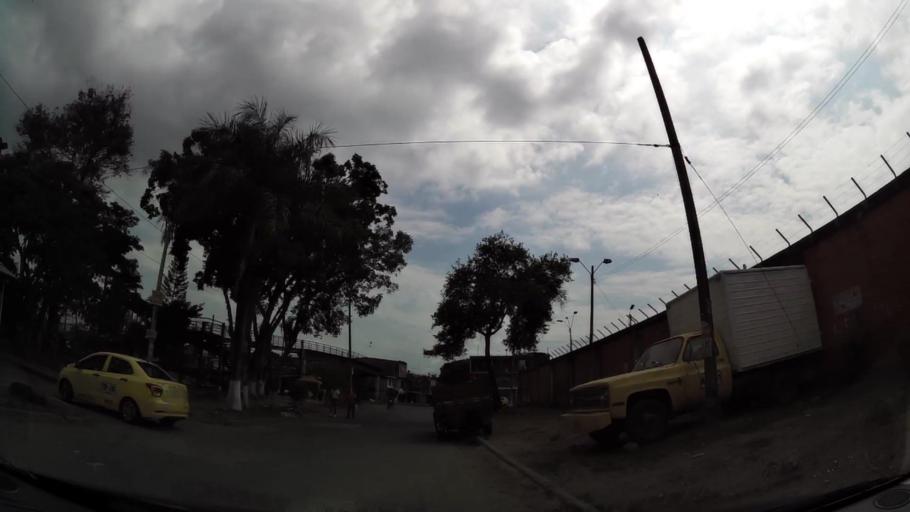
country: CO
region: Valle del Cauca
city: Cali
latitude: 3.4866
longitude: -76.4873
